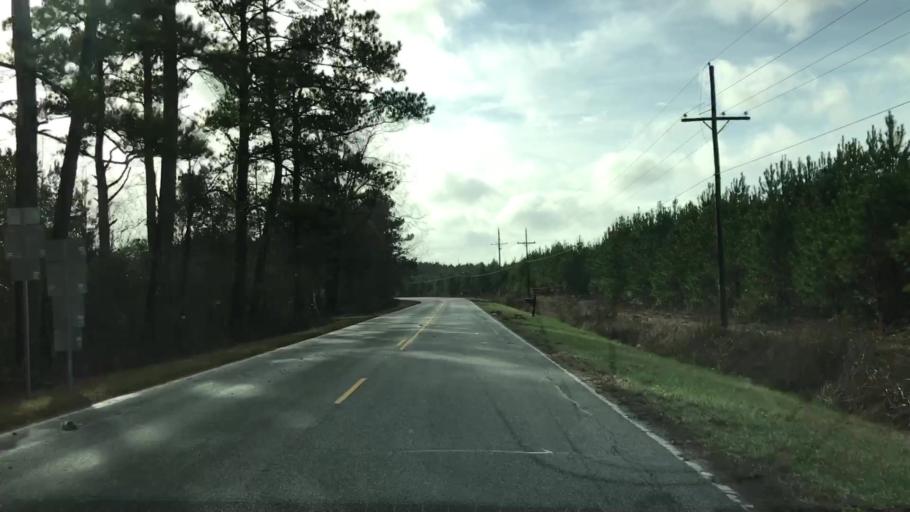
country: US
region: South Carolina
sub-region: Williamsburg County
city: Andrews
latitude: 33.4201
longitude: -79.5995
